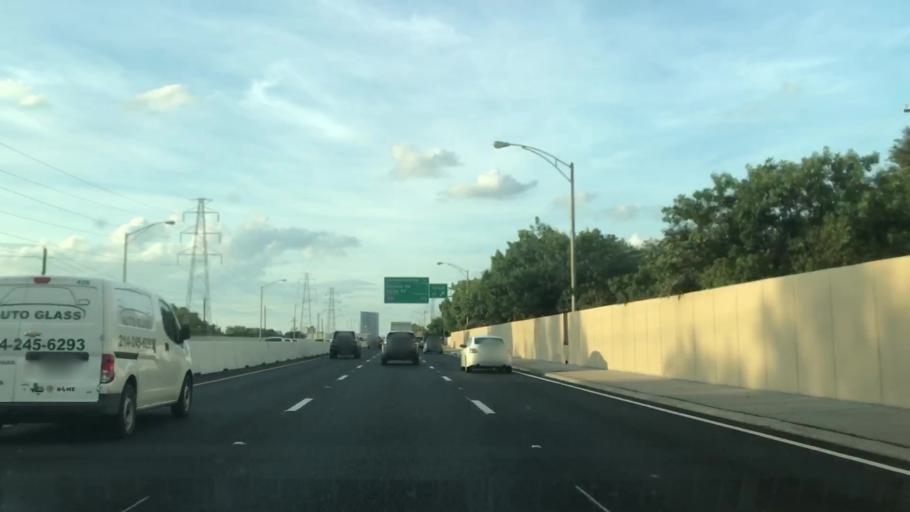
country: US
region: Texas
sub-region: Dallas County
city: University Park
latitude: 32.9049
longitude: -96.8128
